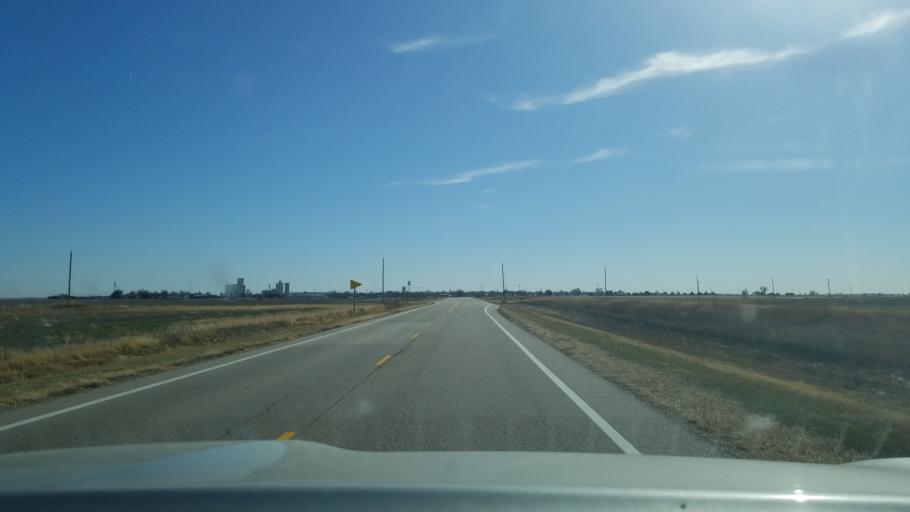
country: US
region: Kansas
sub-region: Kiowa County
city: Greensburg
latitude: 37.5603
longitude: -99.6502
